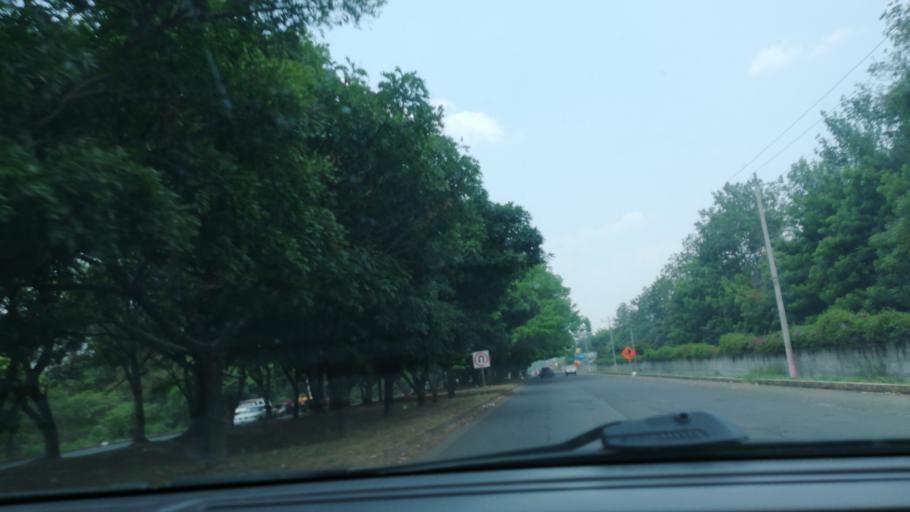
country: SV
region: Santa Ana
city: Chalchuapa
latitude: 13.9879
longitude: -89.6477
